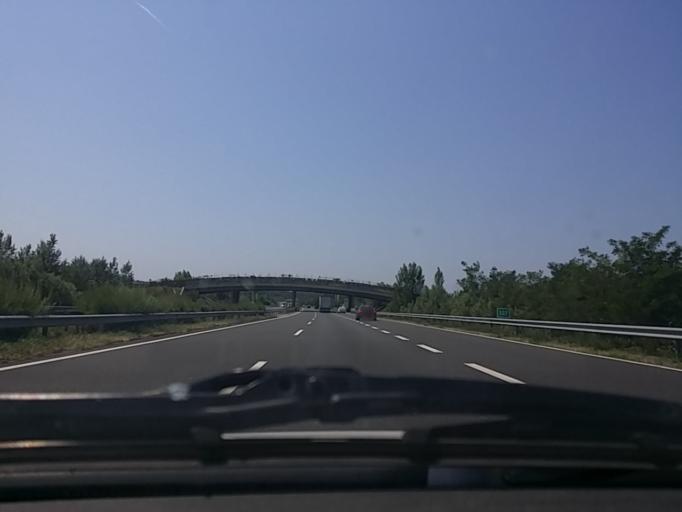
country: HU
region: Somogy
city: Balatonlelle
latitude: 46.7801
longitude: 17.7251
